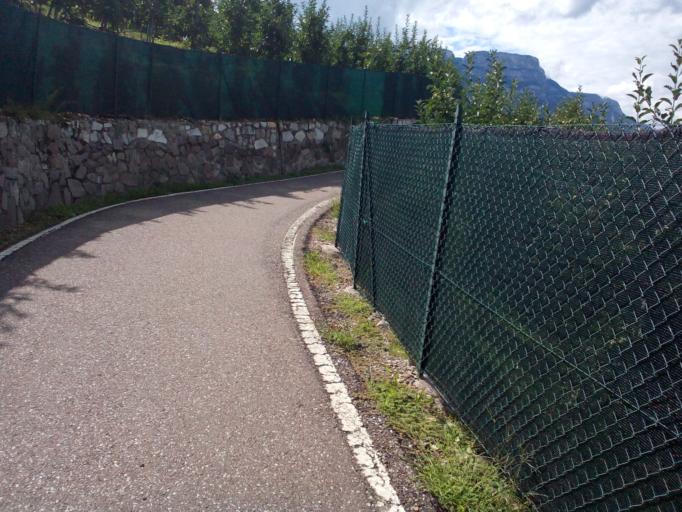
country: IT
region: Trentino-Alto Adige
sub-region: Bolzano
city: Cornaiano
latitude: 46.4766
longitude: 11.3002
